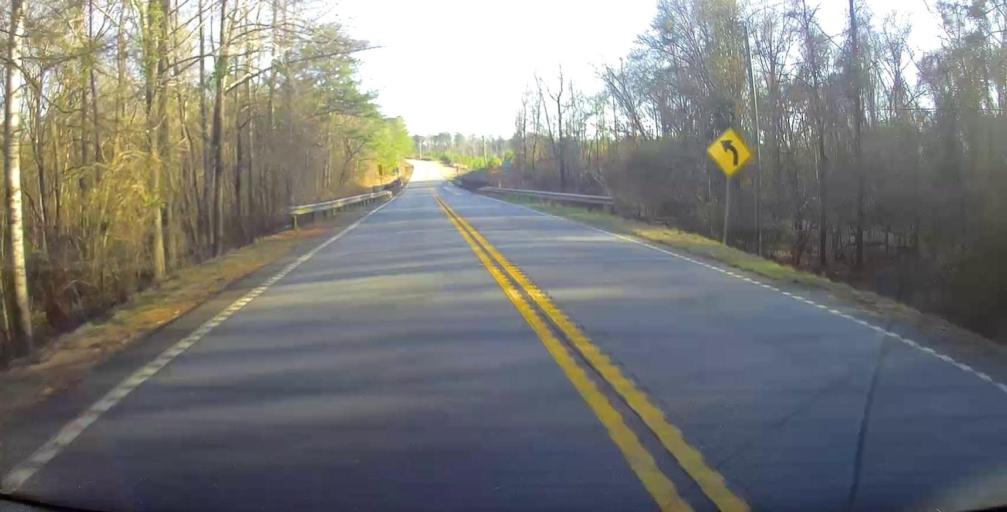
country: US
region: Alabama
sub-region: Chambers County
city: Valley
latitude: 32.7967
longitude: -85.1024
